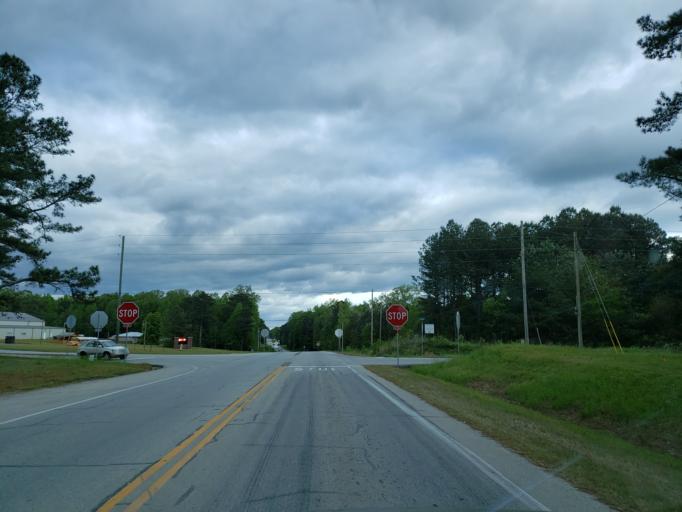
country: US
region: Georgia
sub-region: Haralson County
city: Buchanan
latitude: 33.8167
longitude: -85.1006
